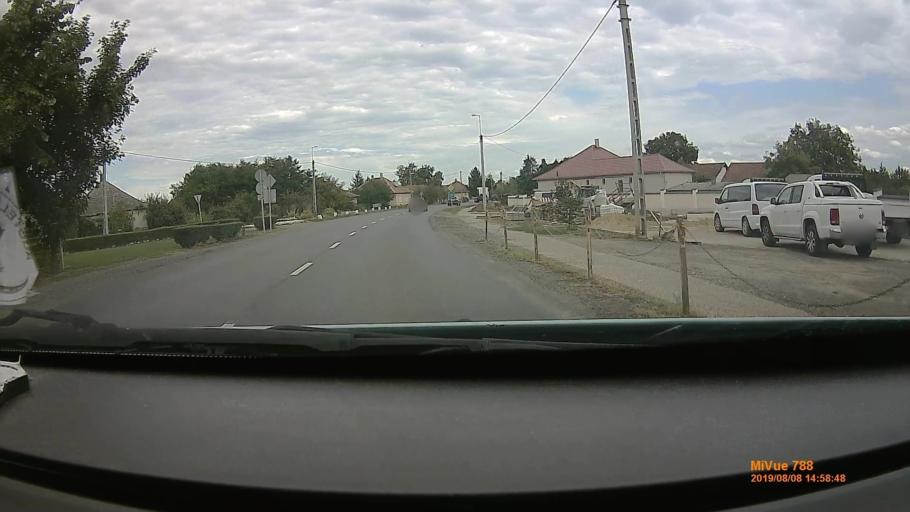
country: HU
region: Szabolcs-Szatmar-Bereg
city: Kocsord
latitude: 47.9433
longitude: 22.3622
